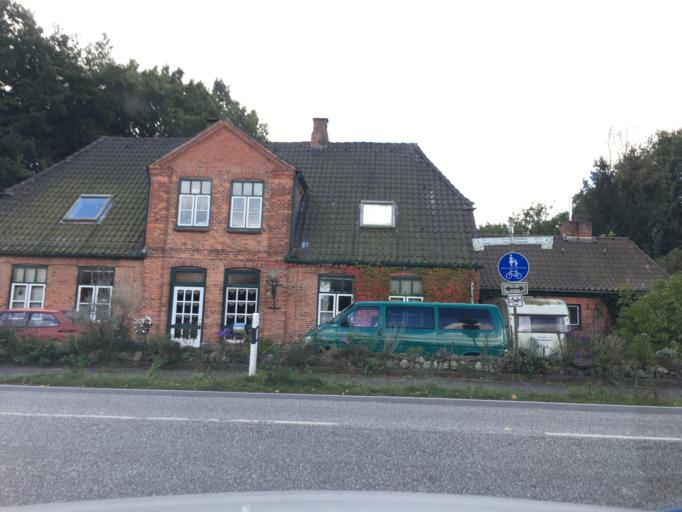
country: DE
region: Schleswig-Holstein
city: Rodenbek
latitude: 54.3038
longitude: 10.0123
